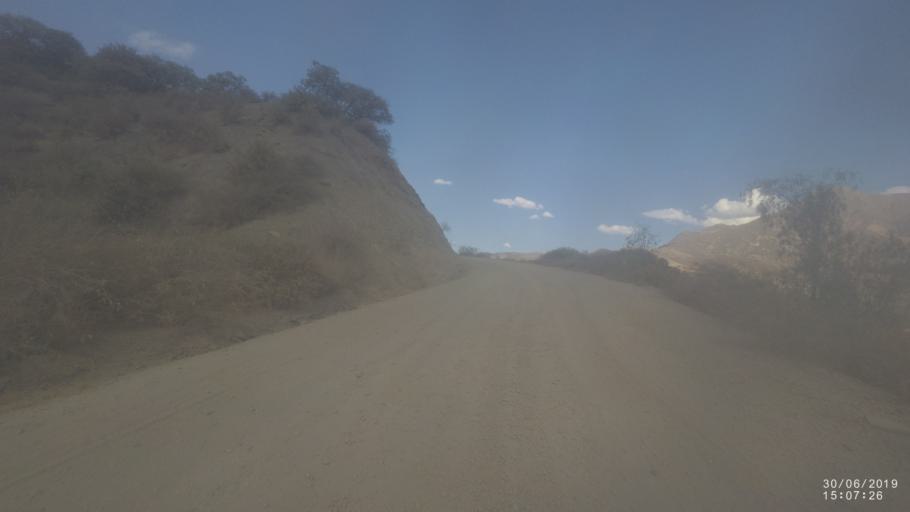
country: BO
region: Cochabamba
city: Irpa Irpa
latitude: -17.7306
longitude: -66.3066
